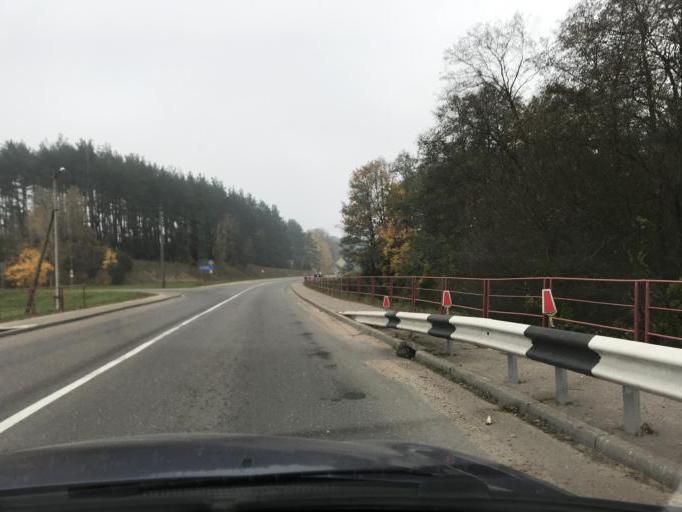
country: BY
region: Grodnenskaya
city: Hrodna
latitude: 53.8113
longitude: 23.8620
